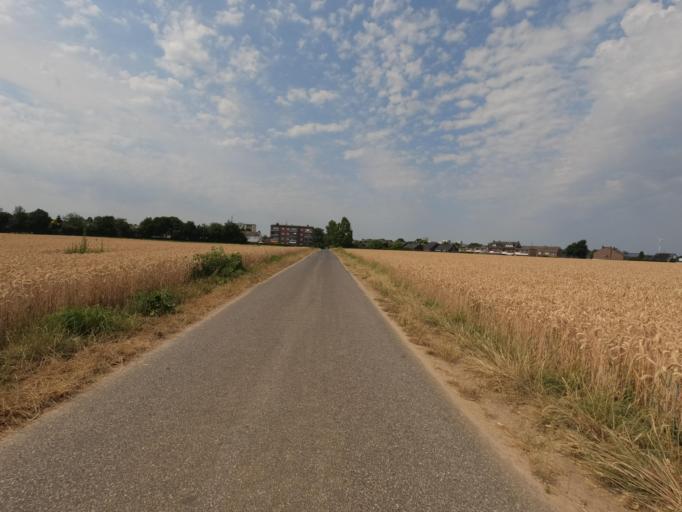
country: DE
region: North Rhine-Westphalia
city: Siersdorf
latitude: 50.9209
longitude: 6.2153
